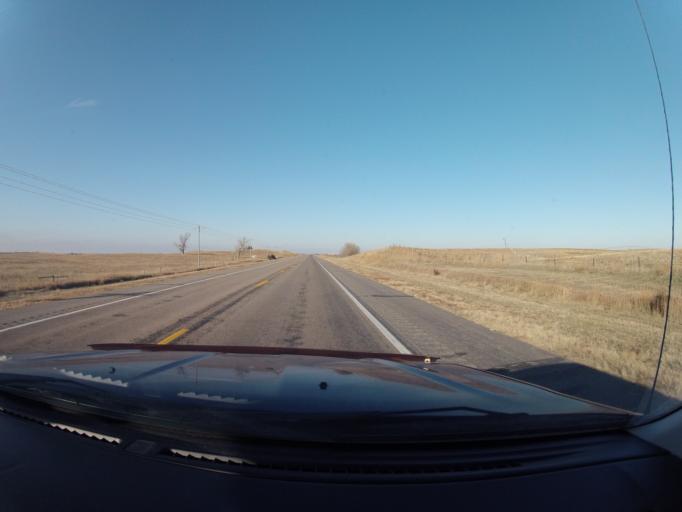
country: US
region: Nebraska
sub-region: Kearney County
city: Minden
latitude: 40.6129
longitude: -98.9515
